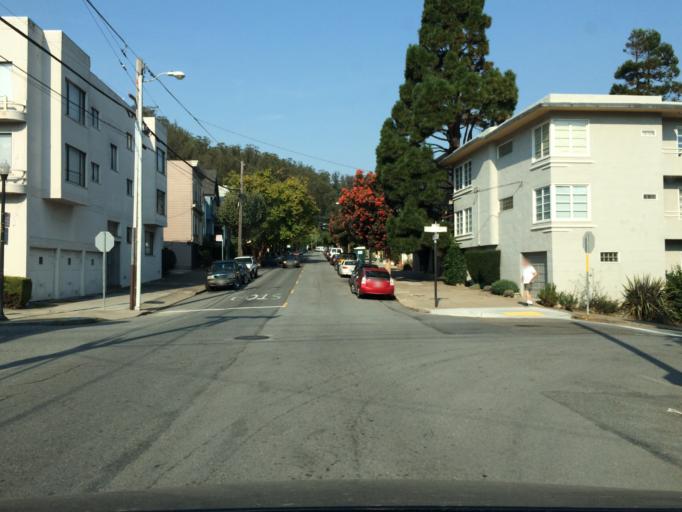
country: US
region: California
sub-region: San Francisco County
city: San Francisco
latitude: 37.7616
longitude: -122.4489
